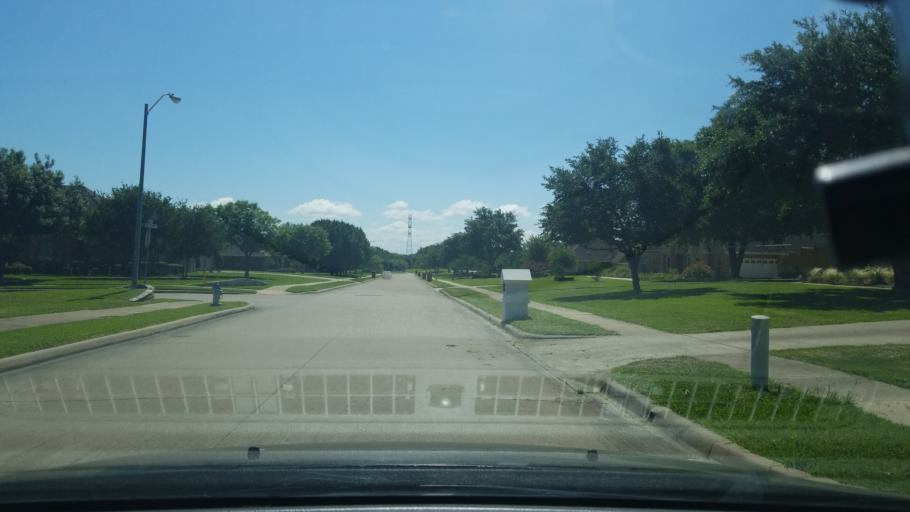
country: US
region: Texas
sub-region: Dallas County
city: Sunnyvale
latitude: 32.7897
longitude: -96.5768
